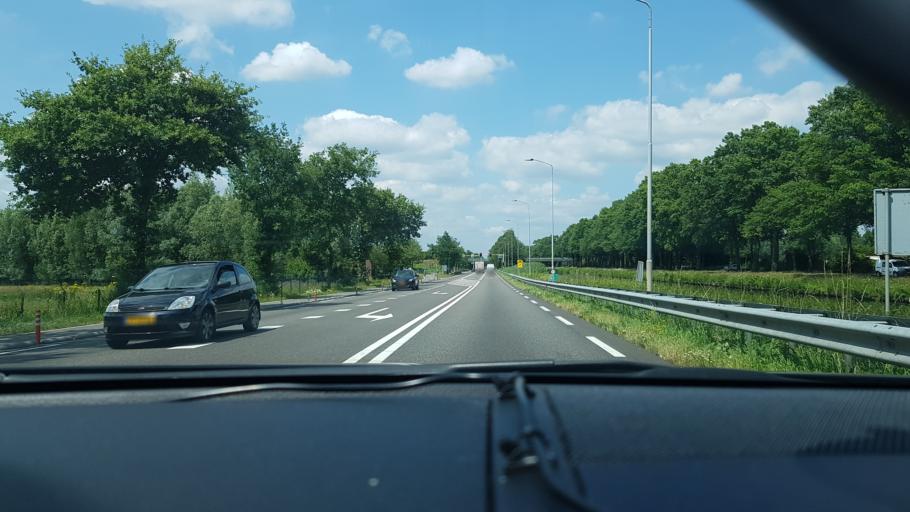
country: NL
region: North Brabant
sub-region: Gemeente Helmond
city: Helmond
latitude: 51.4477
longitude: 5.6839
